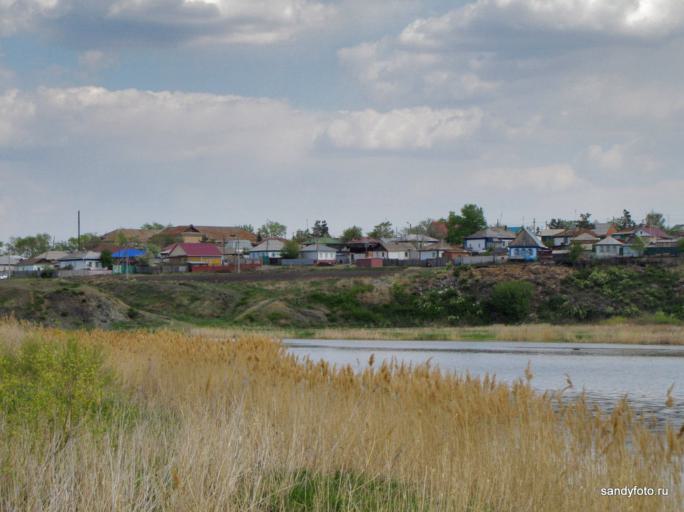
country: RU
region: Chelyabinsk
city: Troitsk
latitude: 54.0881
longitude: 61.5112
